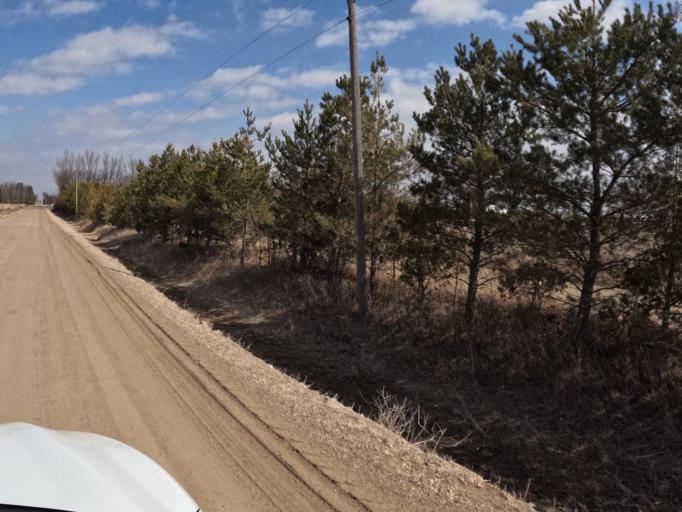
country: CA
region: Ontario
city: Orangeville
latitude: 43.9038
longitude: -80.2516
